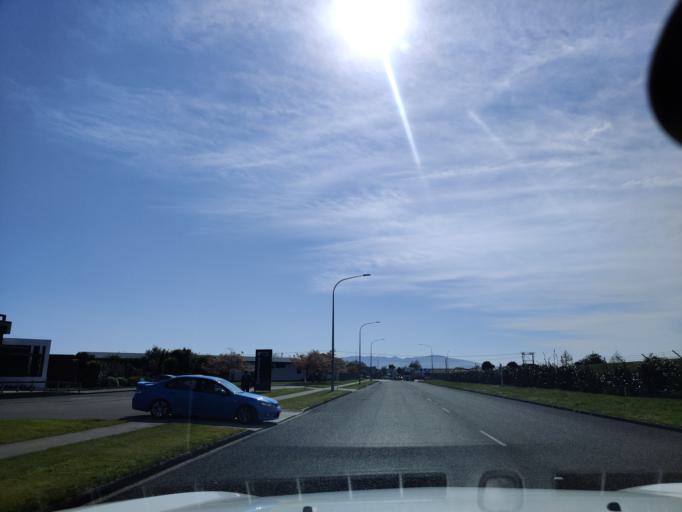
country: NZ
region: Manawatu-Wanganui
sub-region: Palmerston North City
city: Palmerston North
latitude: -40.3316
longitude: 175.6501
